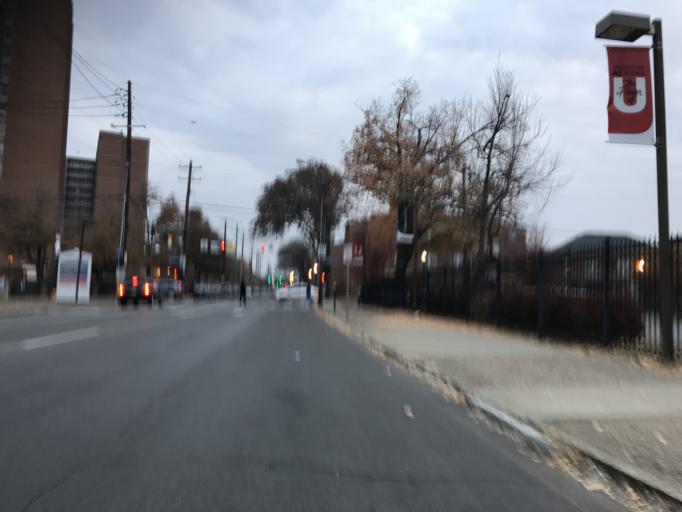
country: US
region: Kentucky
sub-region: Jefferson County
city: Louisville
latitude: 38.2493
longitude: -85.7448
